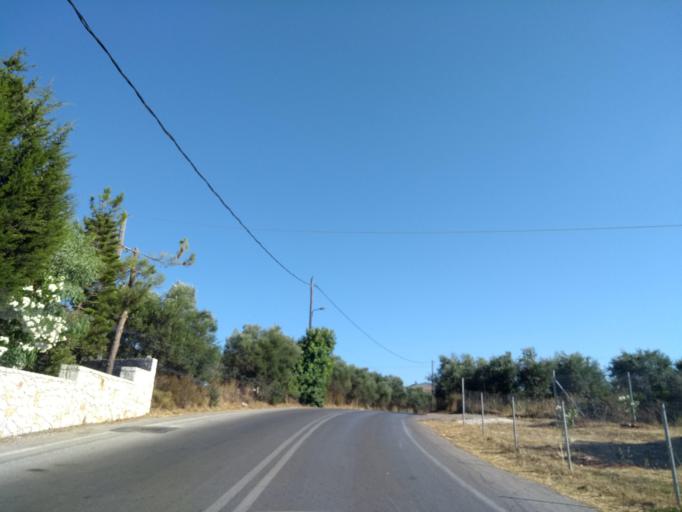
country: GR
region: Crete
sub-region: Nomos Chanias
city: Pithari
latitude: 35.5459
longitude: 24.0825
